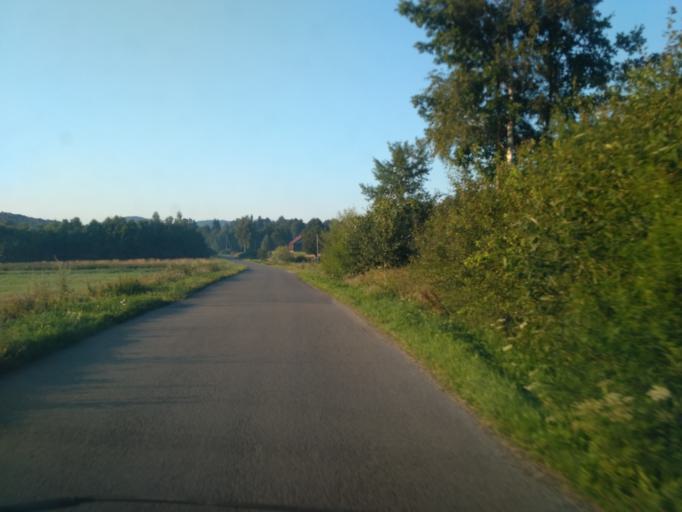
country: PL
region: Subcarpathian Voivodeship
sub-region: Powiat strzyzowski
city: Wysoka Strzyzowska
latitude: 49.7994
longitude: 21.7521
